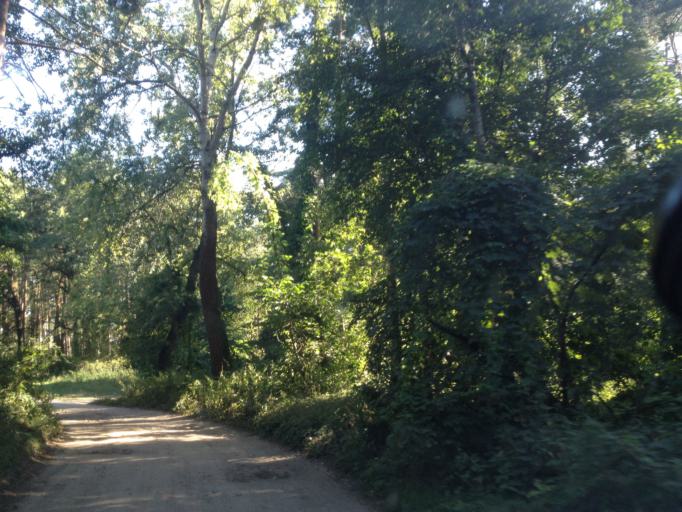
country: PL
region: Greater Poland Voivodeship
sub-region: Powiat sredzki
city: Zaniemysl
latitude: 52.1037
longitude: 17.1323
